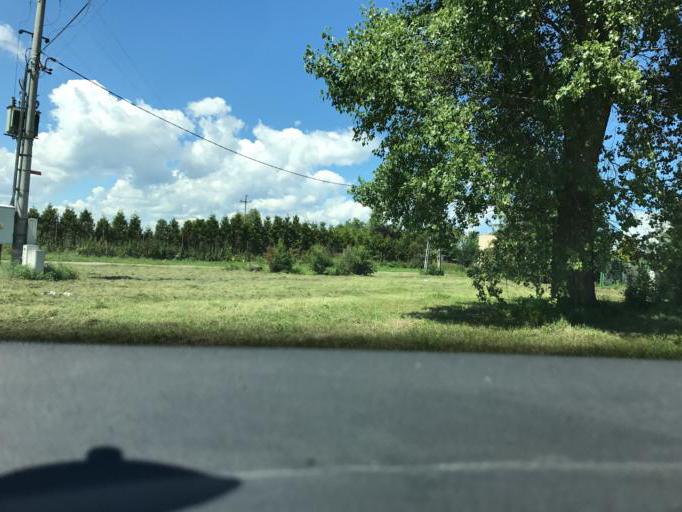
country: PL
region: Pomeranian Voivodeship
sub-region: Gdansk
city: Gdansk
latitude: 54.3313
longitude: 18.7288
